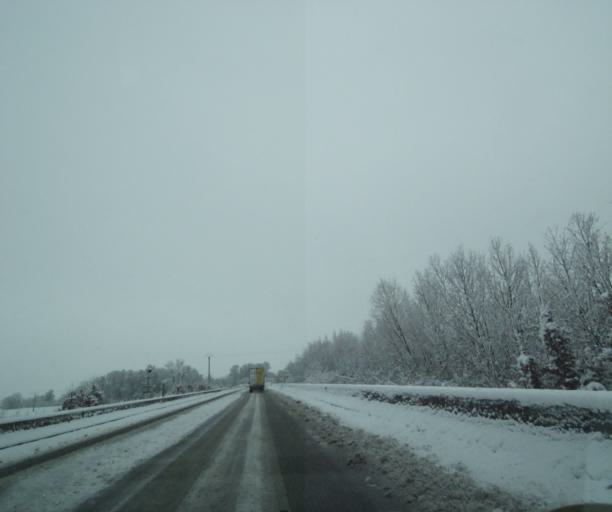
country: FR
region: Champagne-Ardenne
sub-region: Departement de la Haute-Marne
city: Saint-Dizier
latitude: 48.5892
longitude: 4.8907
